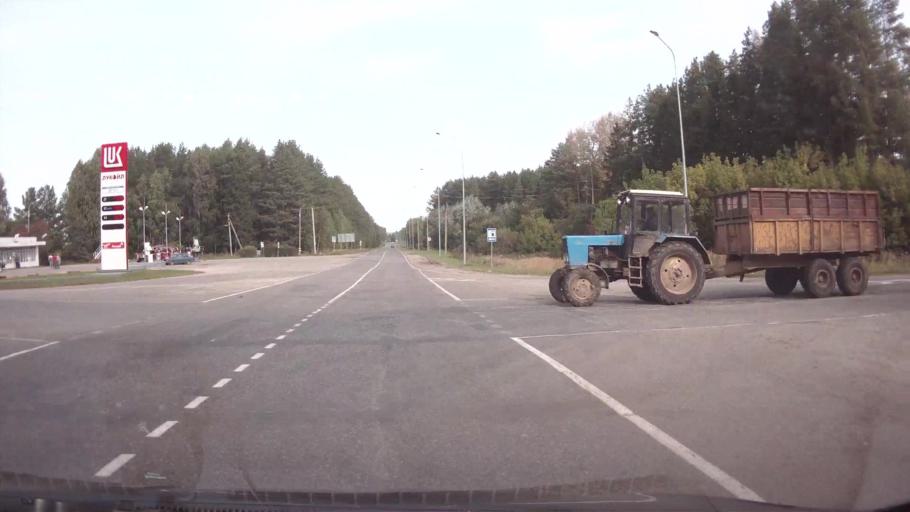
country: RU
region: Mariy-El
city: Kuzhener
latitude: 56.9853
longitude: 48.7450
